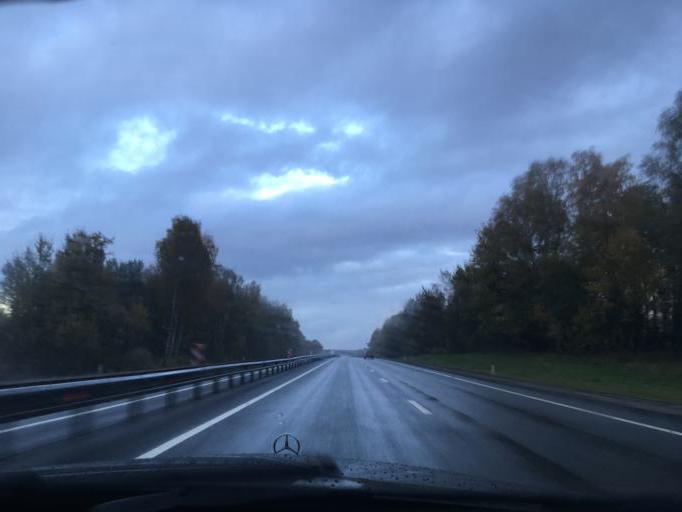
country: RU
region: Smolensk
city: Yartsevo
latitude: 55.0584
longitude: 32.5612
